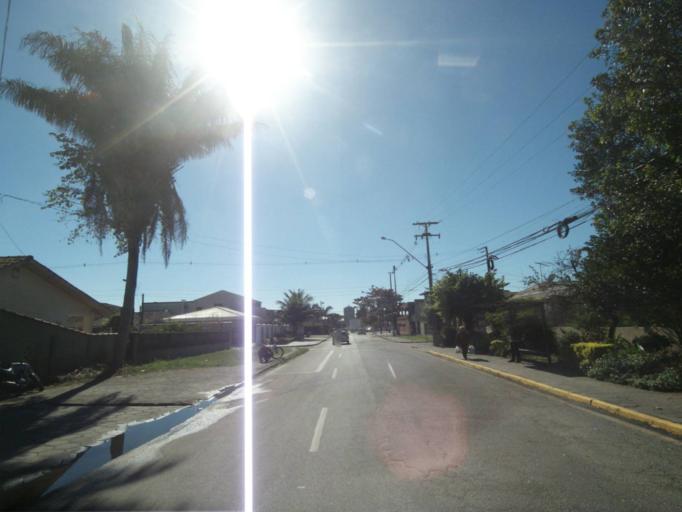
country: BR
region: Parana
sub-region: Paranagua
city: Paranagua
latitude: -25.5276
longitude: -48.5231
